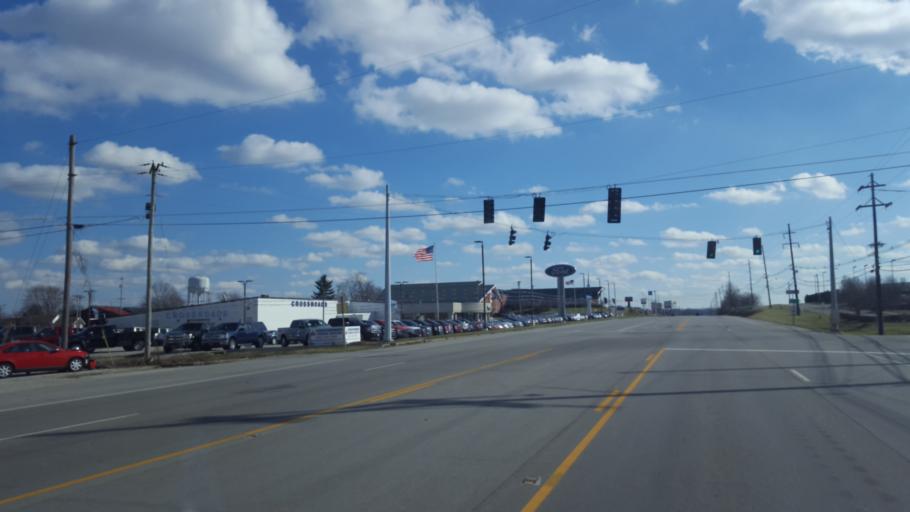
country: US
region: Kentucky
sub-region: Franklin County
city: Frankfort
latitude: 38.1862
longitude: -84.8199
